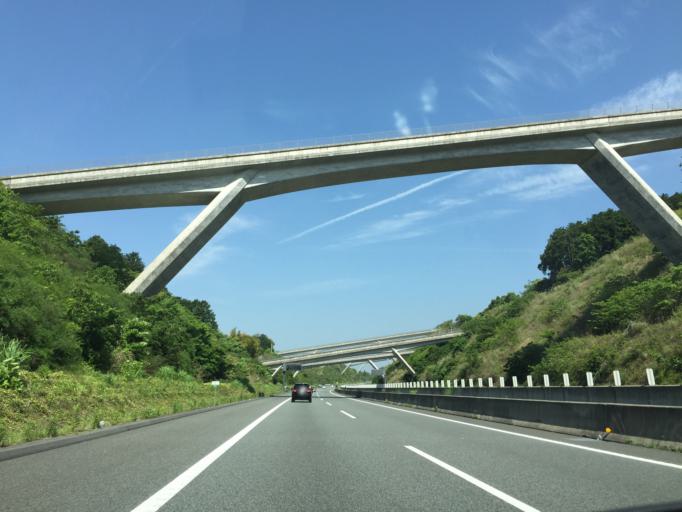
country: JP
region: Shizuoka
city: Fuji
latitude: 35.1636
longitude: 138.7591
